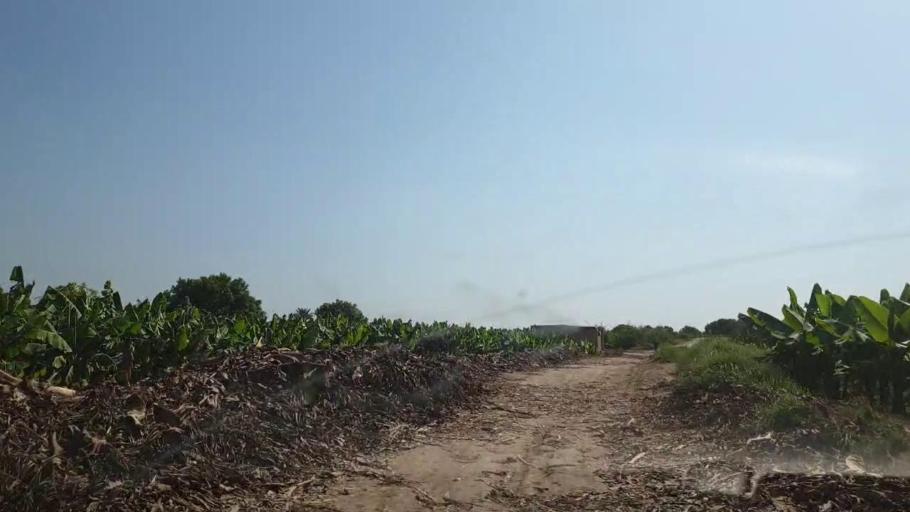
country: PK
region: Sindh
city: Tando Jam
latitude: 25.3719
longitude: 68.5809
